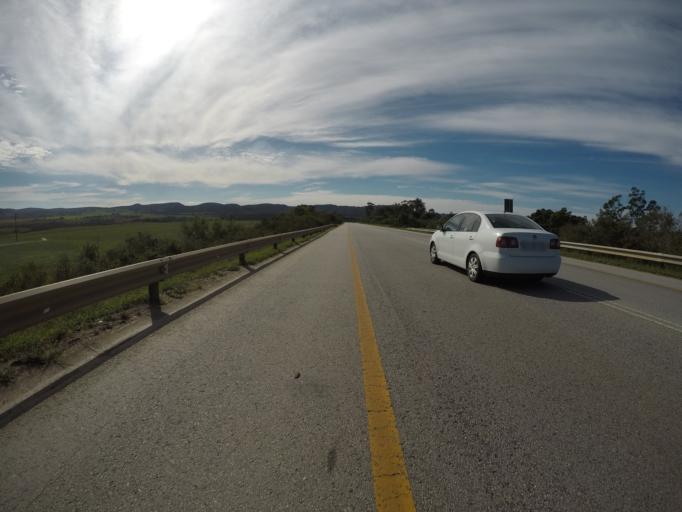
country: ZA
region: Eastern Cape
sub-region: Cacadu District Municipality
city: Jeffrey's Bay
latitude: -33.8944
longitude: 25.1283
